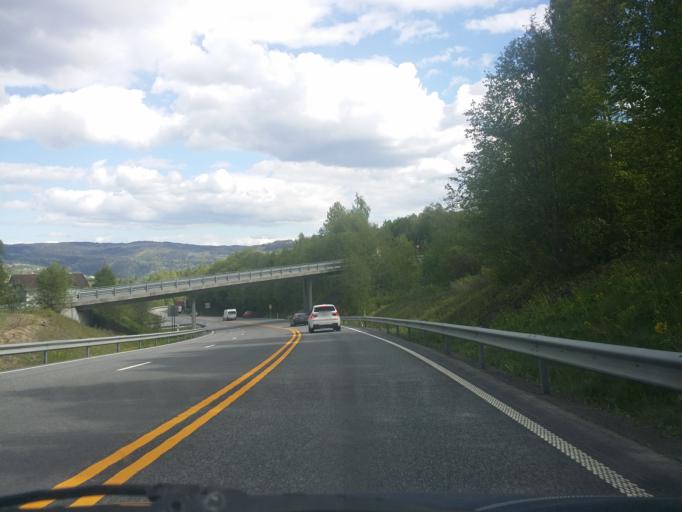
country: NO
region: Oppland
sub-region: Lunner
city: Roa
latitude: 60.2961
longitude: 10.5920
